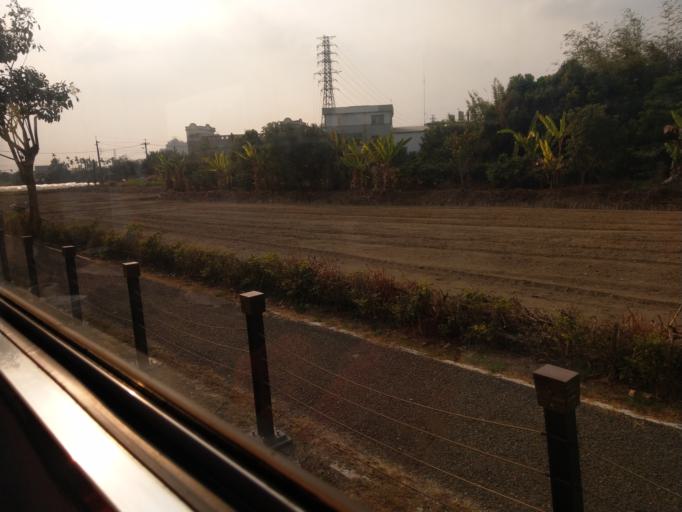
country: TW
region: Taiwan
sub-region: Chiayi
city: Jiayi Shi
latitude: 23.5065
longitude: 120.5343
